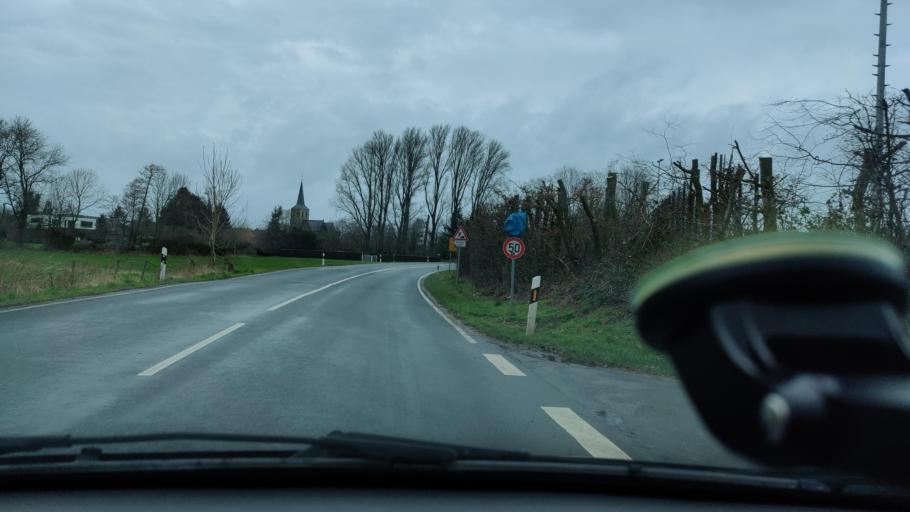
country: DE
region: North Rhine-Westphalia
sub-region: Regierungsbezirk Dusseldorf
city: Kevelaer
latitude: 51.5678
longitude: 6.2973
